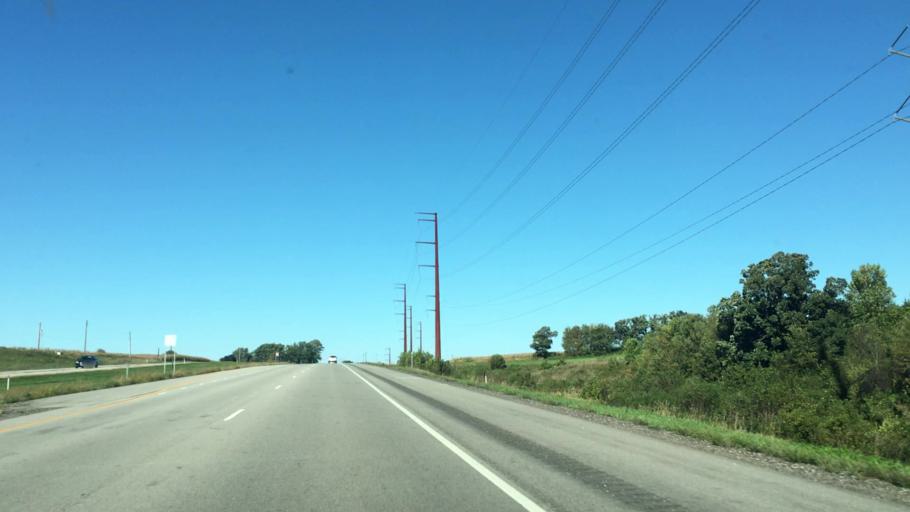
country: US
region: Minnesota
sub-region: Goodhue County
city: Wanamingo
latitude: 44.3349
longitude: -92.7385
